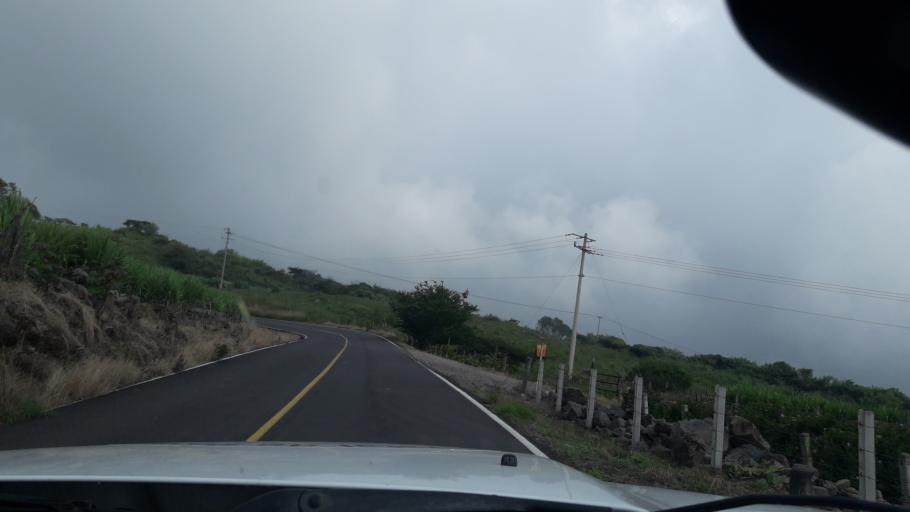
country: MX
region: Colima
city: Queseria
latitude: 19.4080
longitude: -103.6370
